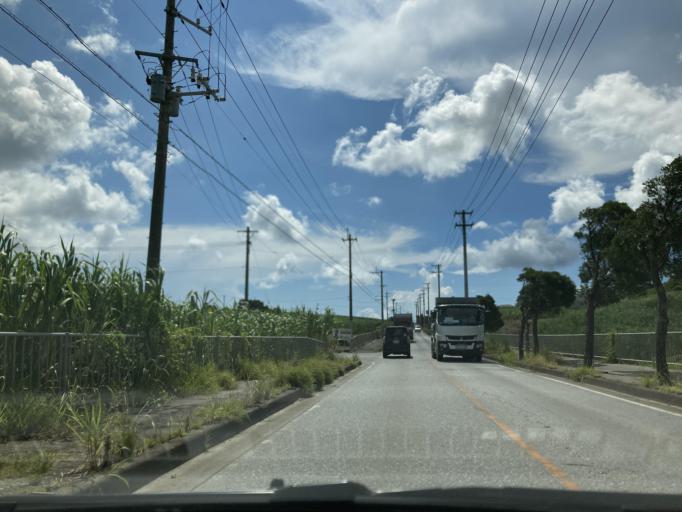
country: JP
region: Okinawa
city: Itoman
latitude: 26.1424
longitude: 127.7275
